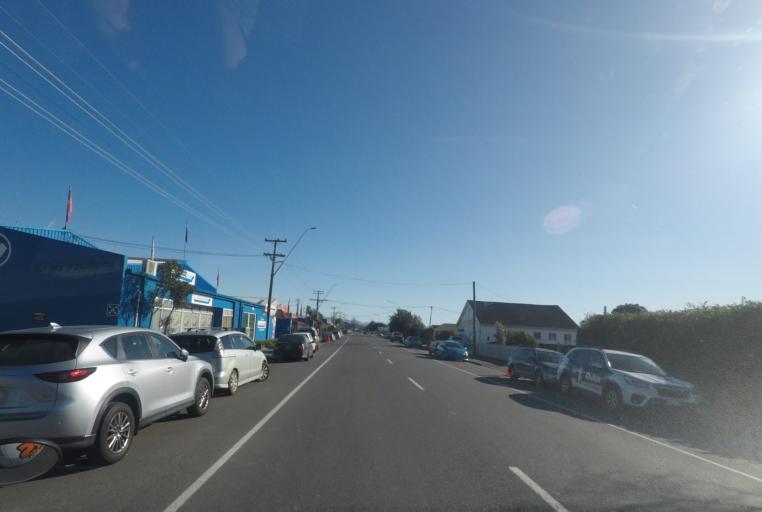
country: NZ
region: Nelson
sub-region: Nelson City
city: Nelson
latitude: -41.2904
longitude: 173.2422
